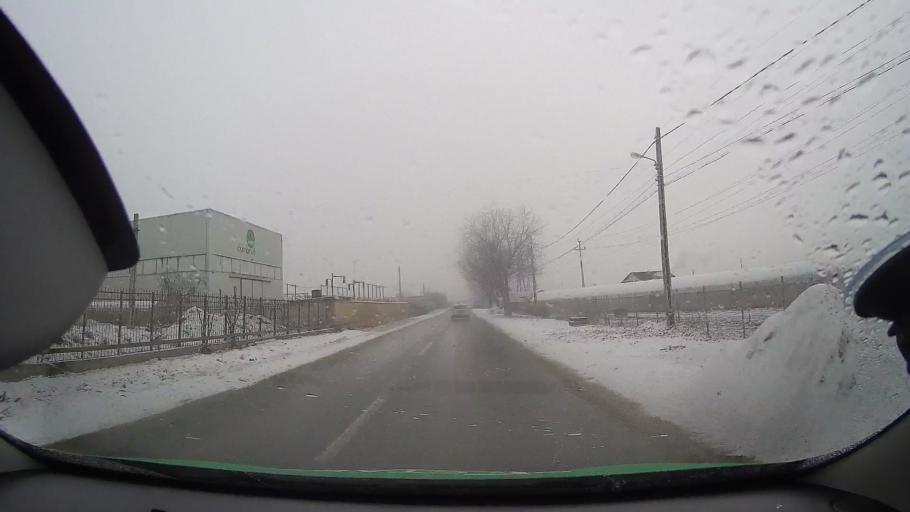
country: RO
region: Alba
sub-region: Municipiul Aiud
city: Aiud
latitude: 46.3053
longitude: 23.7374
